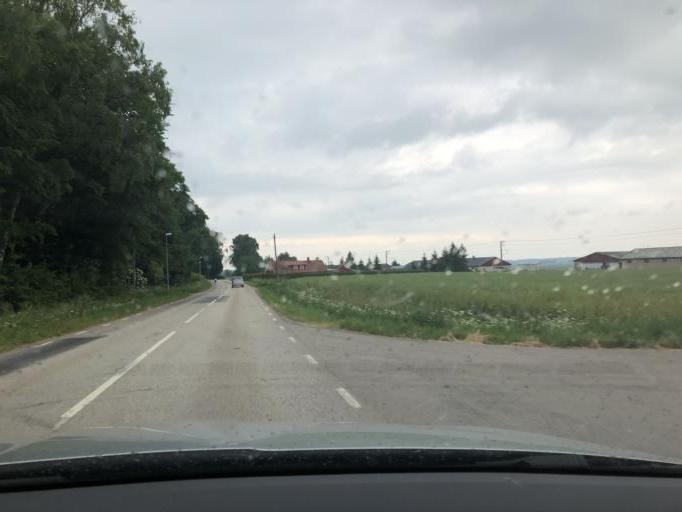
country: SE
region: Blekinge
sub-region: Solvesborgs Kommun
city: Soelvesborg
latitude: 56.0953
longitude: 14.6135
